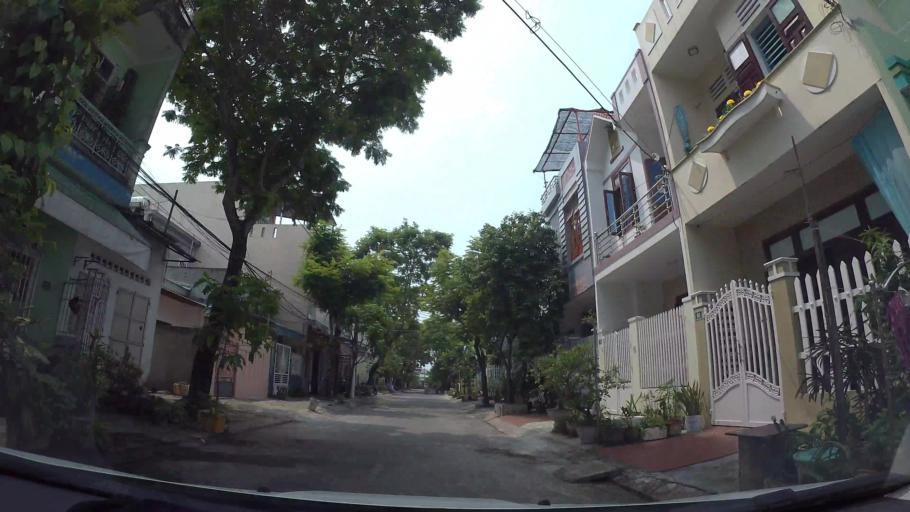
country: VN
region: Da Nang
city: Son Tra
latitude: 16.0990
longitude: 108.2482
